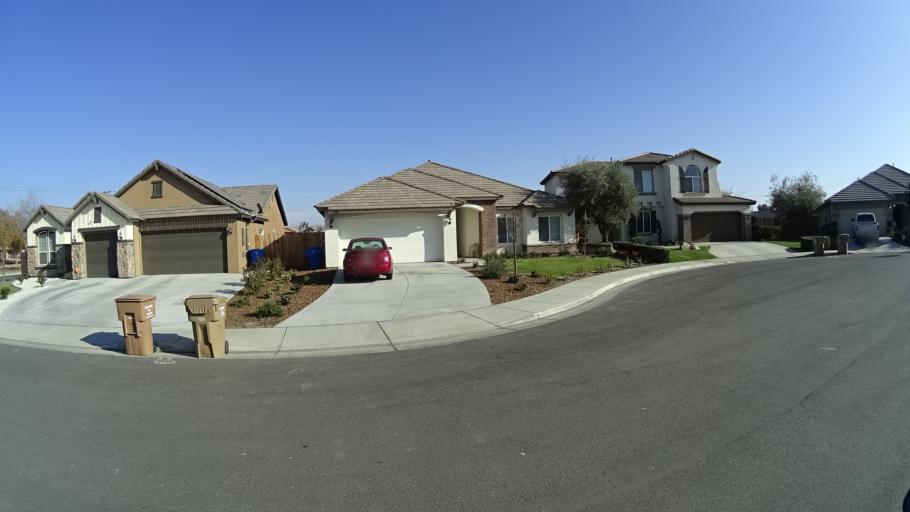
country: US
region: California
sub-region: Kern County
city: Greenacres
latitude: 35.3772
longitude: -119.1094
